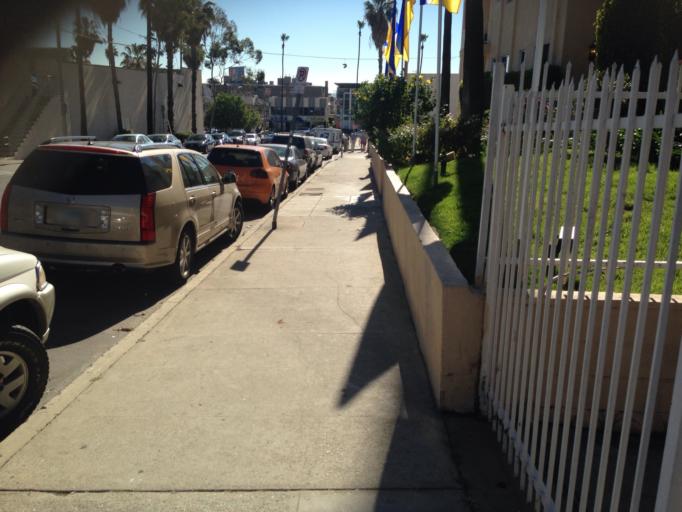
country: US
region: California
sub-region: Los Angeles County
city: West Hollywood
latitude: 34.0991
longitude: -118.3490
